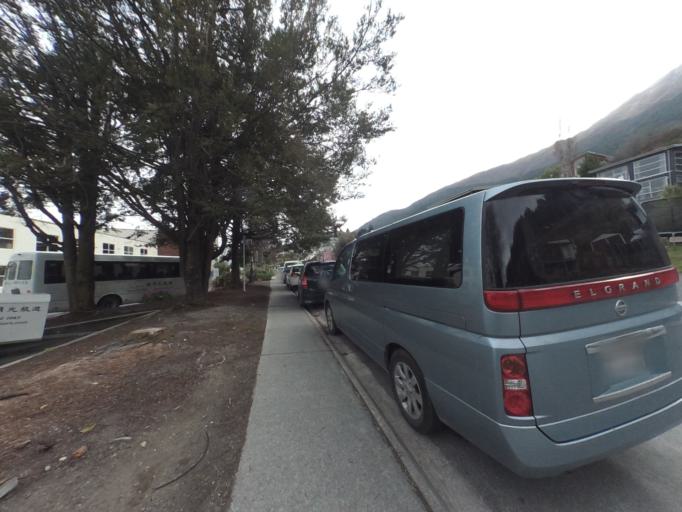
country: NZ
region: Otago
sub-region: Queenstown-Lakes District
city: Queenstown
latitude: -45.0385
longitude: 168.6386
